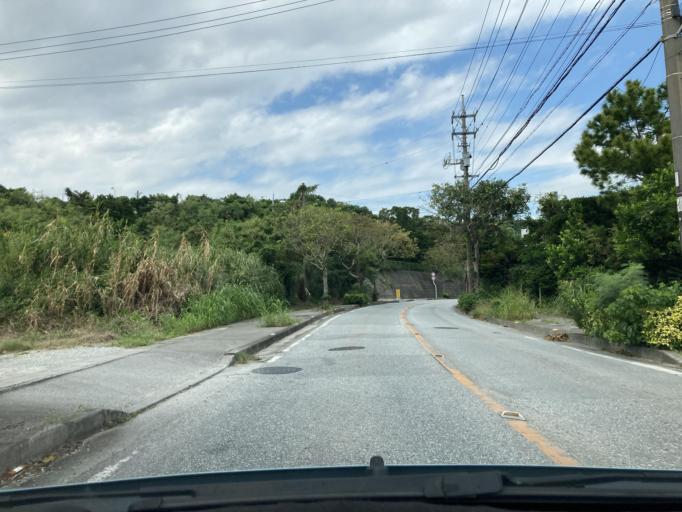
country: JP
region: Okinawa
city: Ginowan
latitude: 26.2739
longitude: 127.7811
